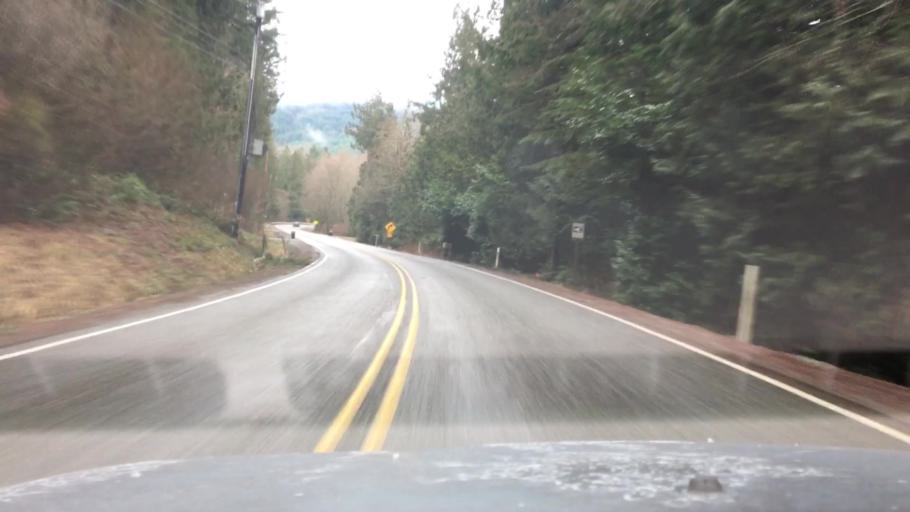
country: US
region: Washington
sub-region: Whatcom County
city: Sudden Valley
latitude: 48.6409
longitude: -122.3193
